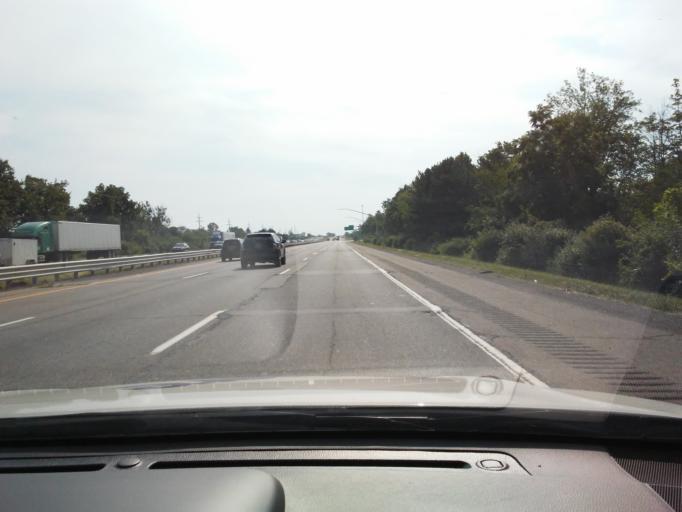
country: US
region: Michigan
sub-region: Oakland County
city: Clawson
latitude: 42.5591
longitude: -83.1408
